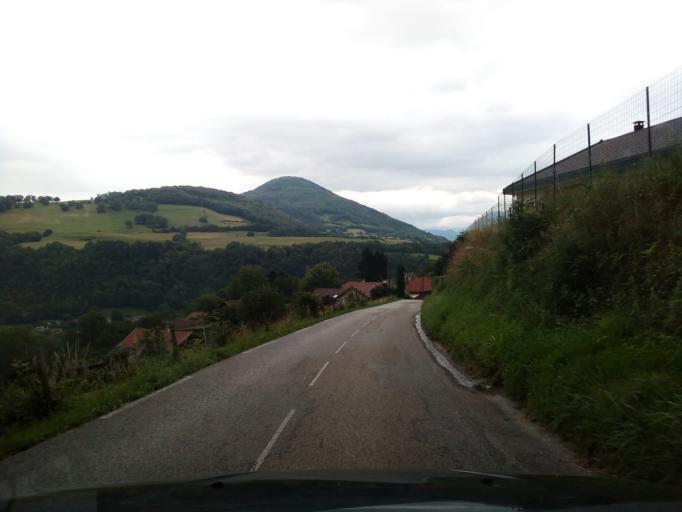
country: FR
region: Rhone-Alpes
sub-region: Departement de l'Isere
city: Vaulnaveys-le-Haut
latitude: 45.1347
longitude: 5.8345
